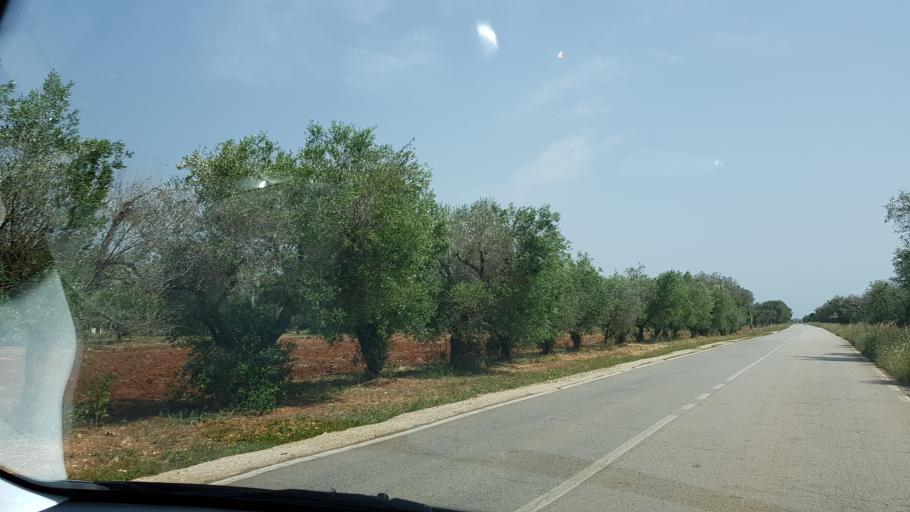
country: IT
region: Apulia
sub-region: Provincia di Brindisi
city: San Pancrazio Salentino
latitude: 40.4569
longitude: 17.8398
